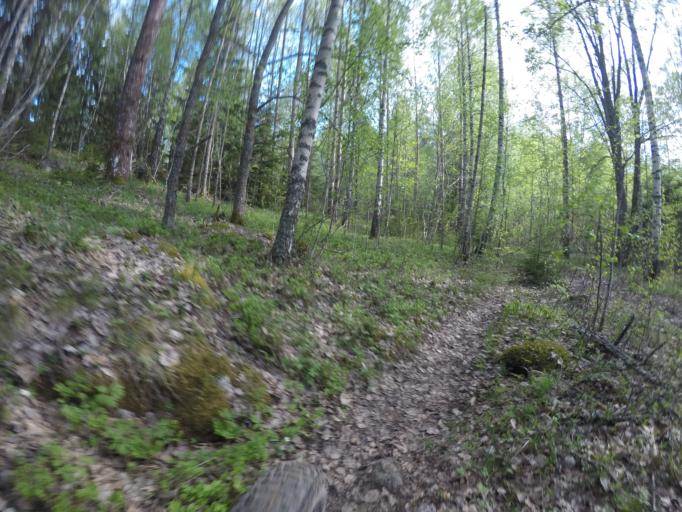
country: SE
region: Vaestmanland
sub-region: Vasteras
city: Vasteras
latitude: 59.6582
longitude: 16.5069
